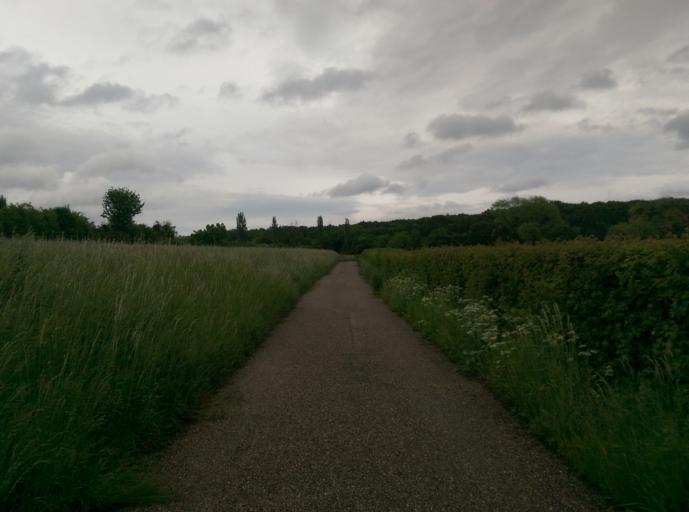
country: LU
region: Luxembourg
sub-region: Canton de Luxembourg
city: Niederanven
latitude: 49.6619
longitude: 6.2549
